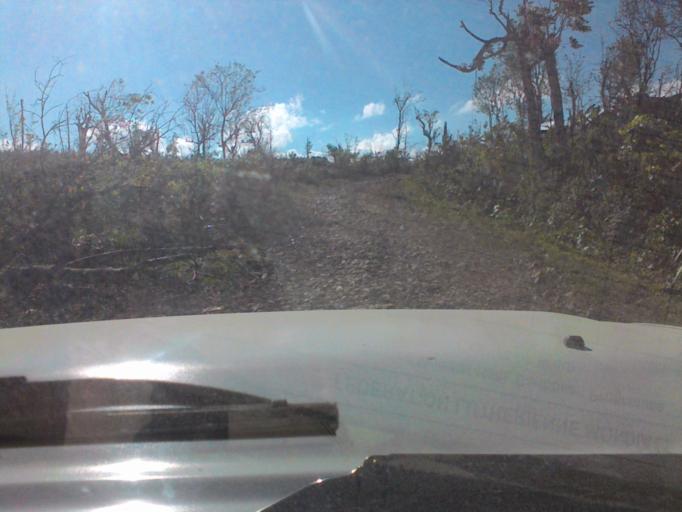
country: HT
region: Grandans
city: Jeremie
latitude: 18.4924
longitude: -74.1073
